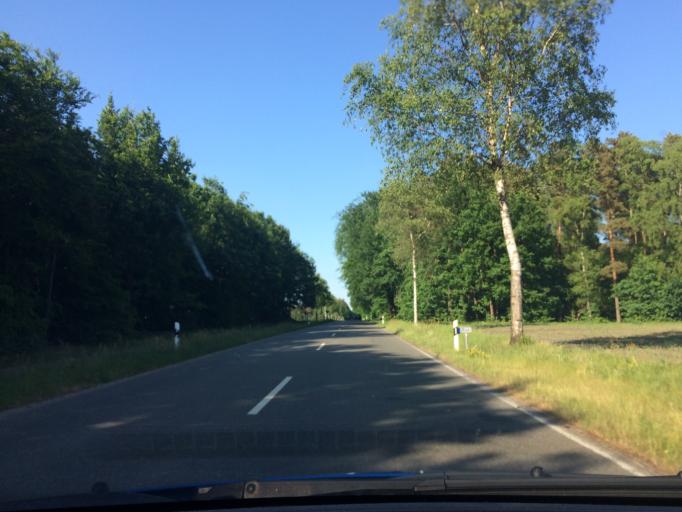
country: DE
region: Lower Saxony
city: Bispingen
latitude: 53.0506
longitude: 9.9426
